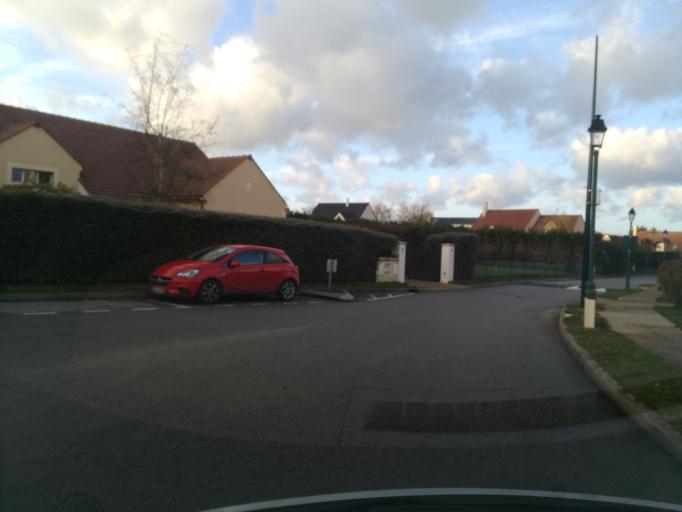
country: FR
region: Ile-de-France
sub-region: Departement des Yvelines
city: Chambourcy
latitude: 48.9055
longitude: 2.0229
